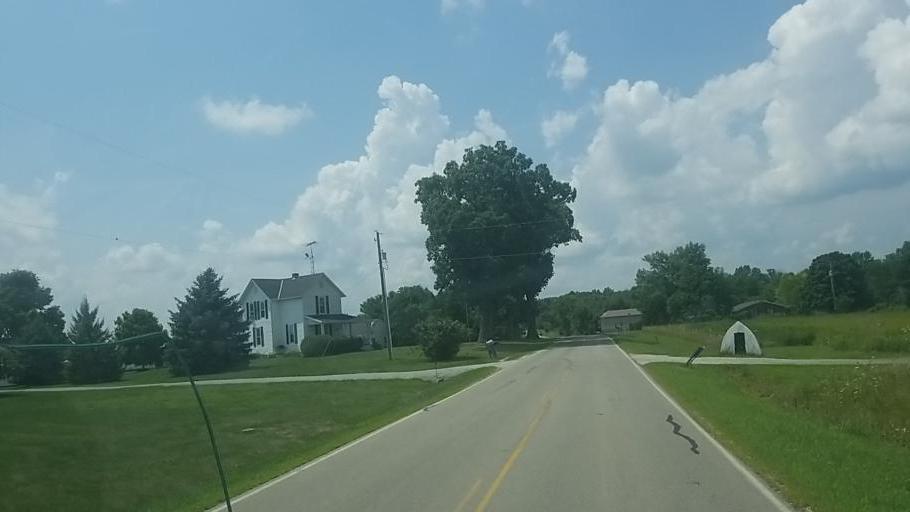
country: US
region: Ohio
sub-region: Crawford County
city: Bucyrus
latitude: 40.7628
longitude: -83.0535
